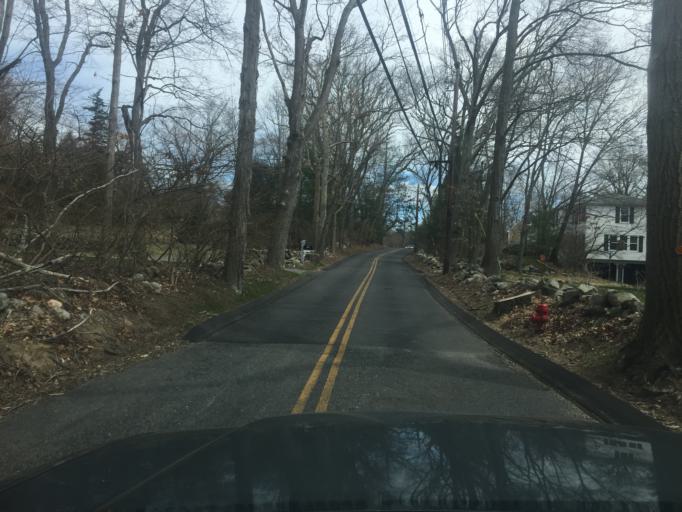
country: US
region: Massachusetts
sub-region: Norfolk County
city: Millis
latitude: 42.1836
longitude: -71.3862
